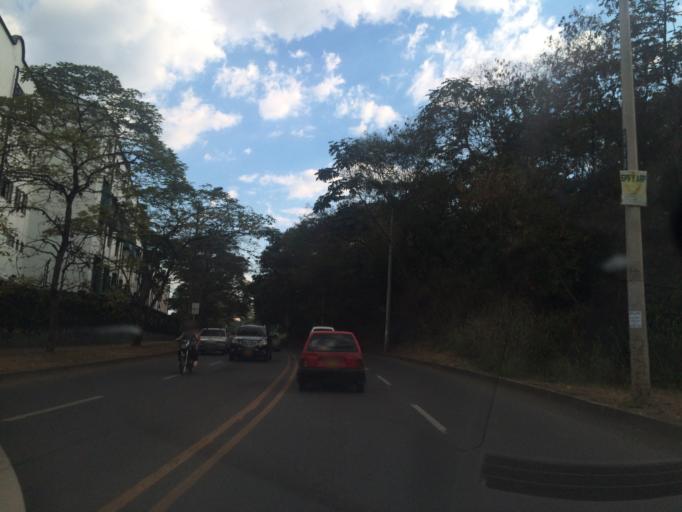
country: CO
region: Valle del Cauca
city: Cali
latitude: 3.4041
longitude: -76.5562
